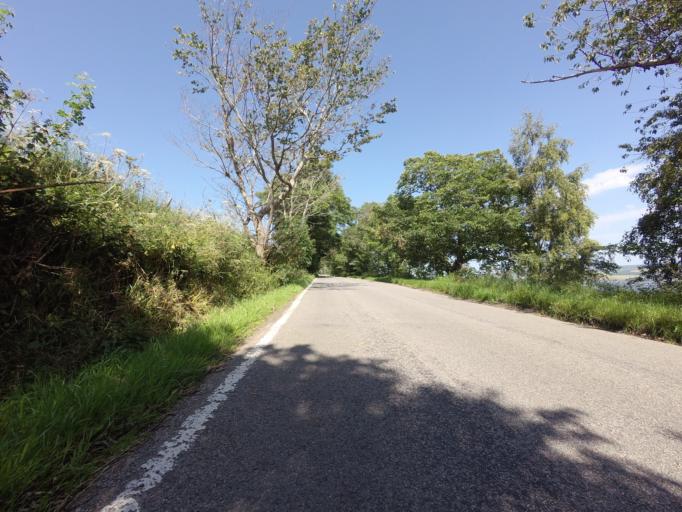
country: GB
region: Scotland
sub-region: Highland
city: Dingwall
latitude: 57.6167
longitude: -4.4063
